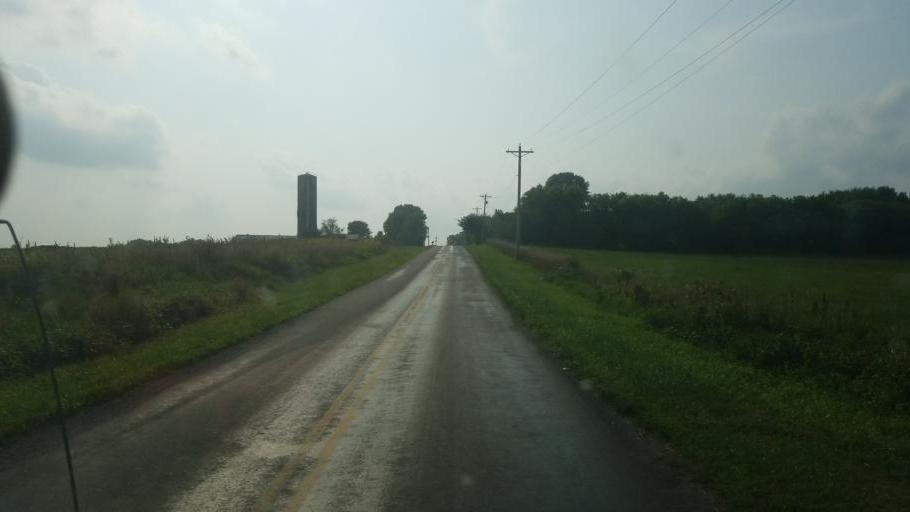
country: US
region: Ohio
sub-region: Medina County
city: Lodi
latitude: 41.0050
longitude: -81.9818
